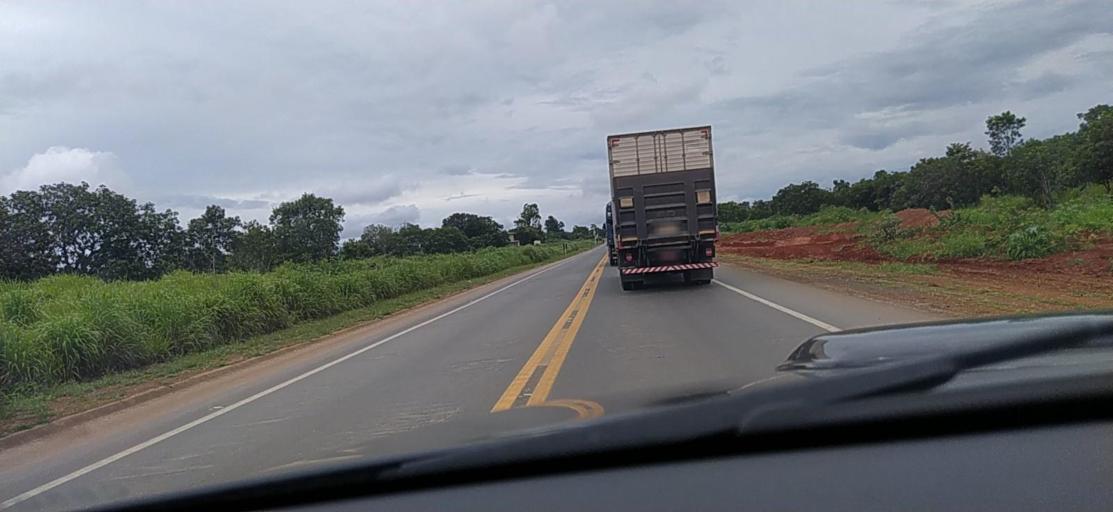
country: BR
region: Minas Gerais
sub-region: Curvelo
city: Curvelo
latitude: -18.7186
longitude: -44.4422
